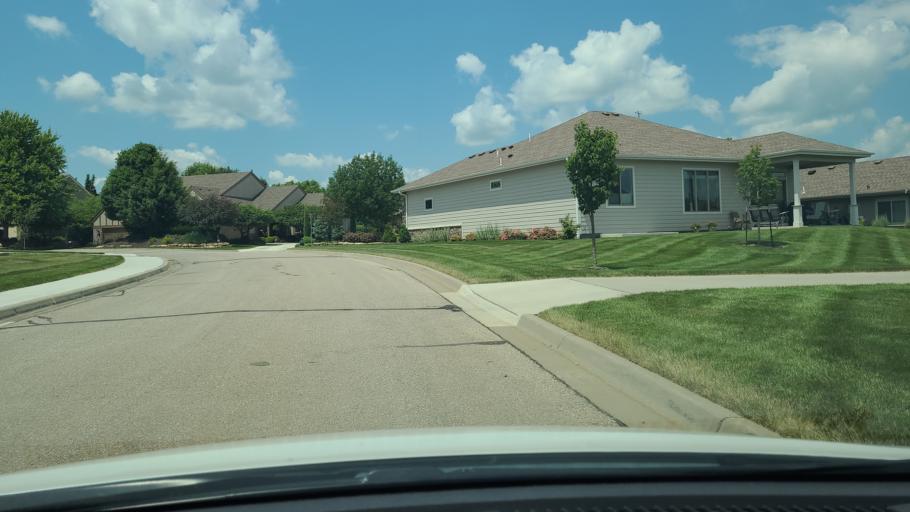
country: US
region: Kansas
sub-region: Douglas County
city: Lawrence
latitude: 38.9835
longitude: -95.3113
